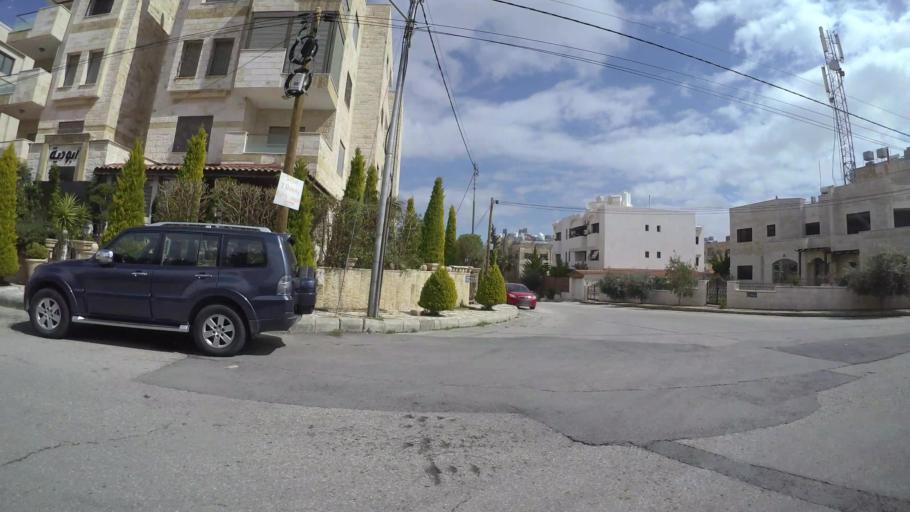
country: JO
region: Amman
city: Wadi as Sir
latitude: 31.9616
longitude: 35.8403
